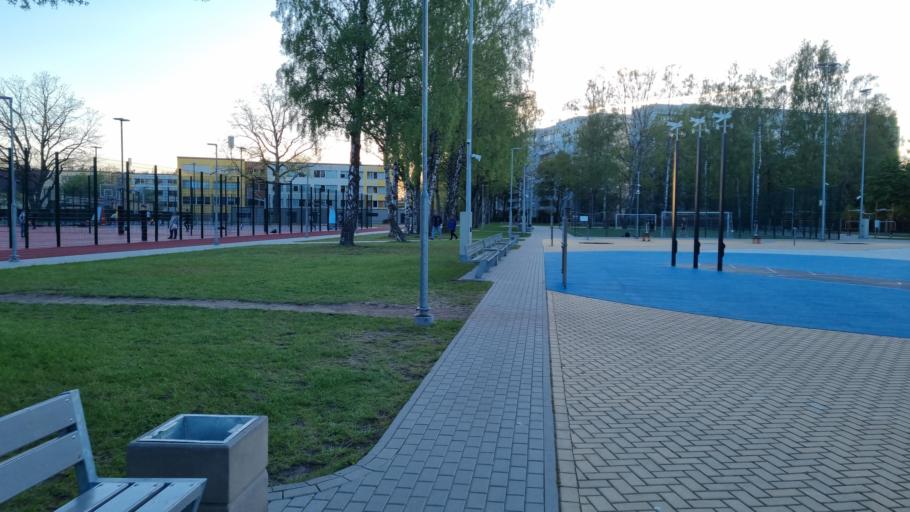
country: LV
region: Marupe
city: Marupe
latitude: 56.9565
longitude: 24.0023
